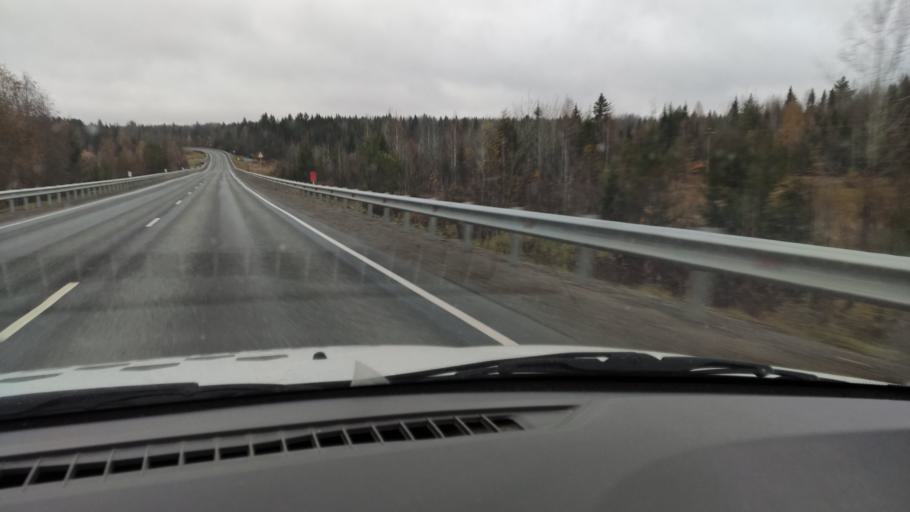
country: RU
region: Kirov
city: Omutninsk
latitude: 58.6920
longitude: 52.1312
